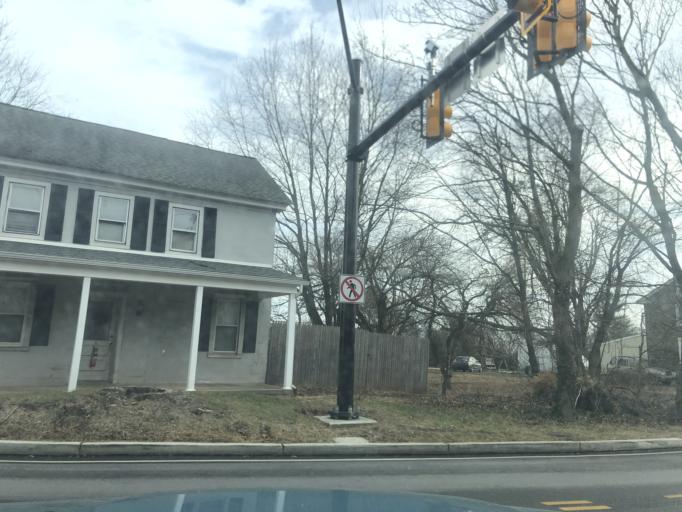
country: US
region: Pennsylvania
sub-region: Montgomery County
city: Harleysville
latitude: 40.2614
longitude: -75.4068
